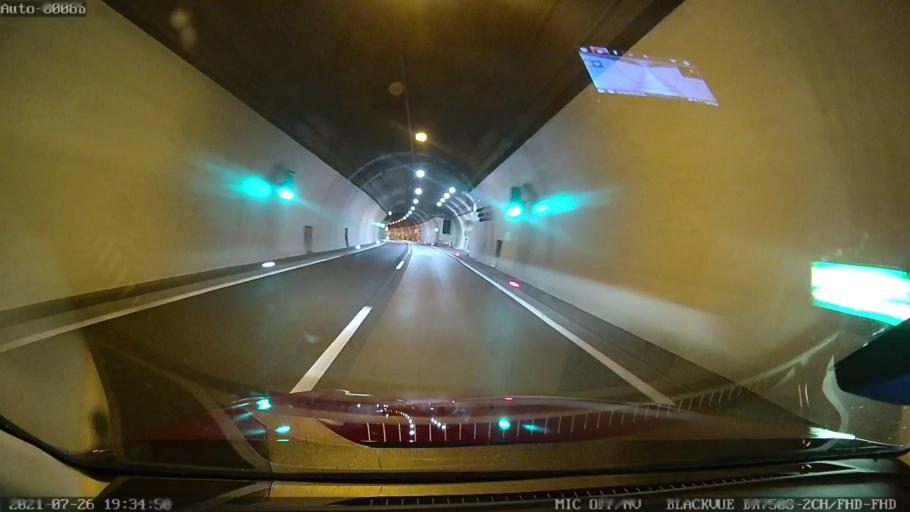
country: AT
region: Upper Austria
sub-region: Politischer Bezirk Kirchdorf an der Krems
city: Rossleithen
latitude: 47.7546
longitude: 14.2291
